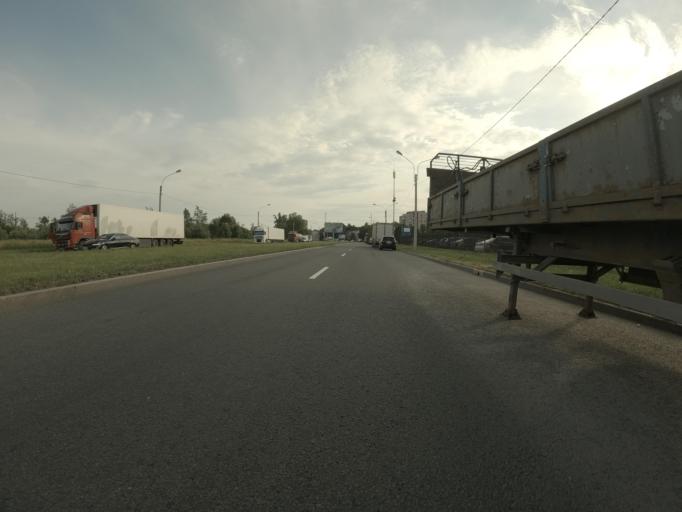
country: RU
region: Leningrad
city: Rybatskoye
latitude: 59.8799
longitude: 30.4841
